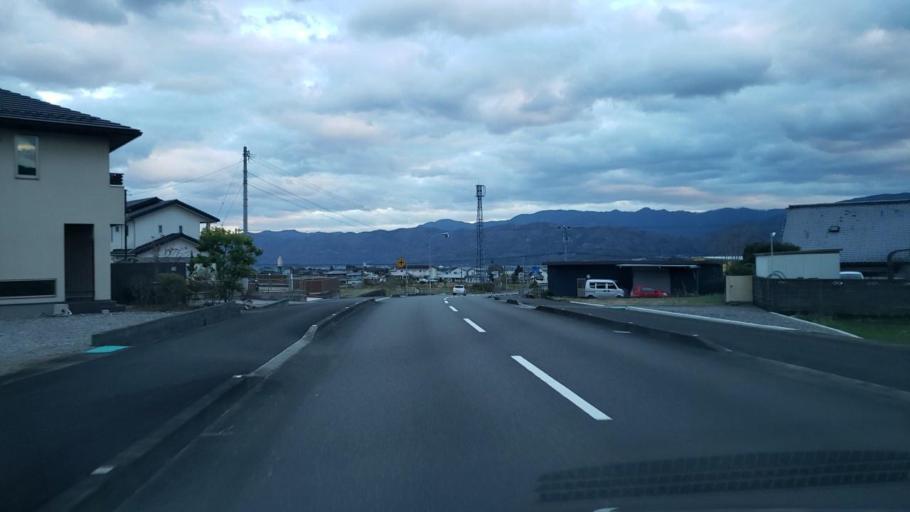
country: JP
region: Tokushima
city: Wakimachi
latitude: 34.0957
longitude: 134.2286
